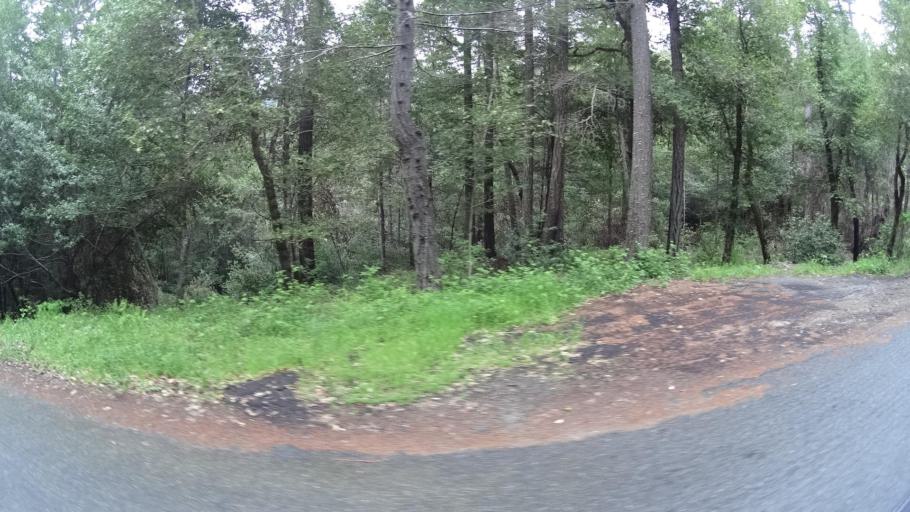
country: US
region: California
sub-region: Siskiyou County
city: Happy Camp
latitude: 41.3667
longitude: -123.5049
